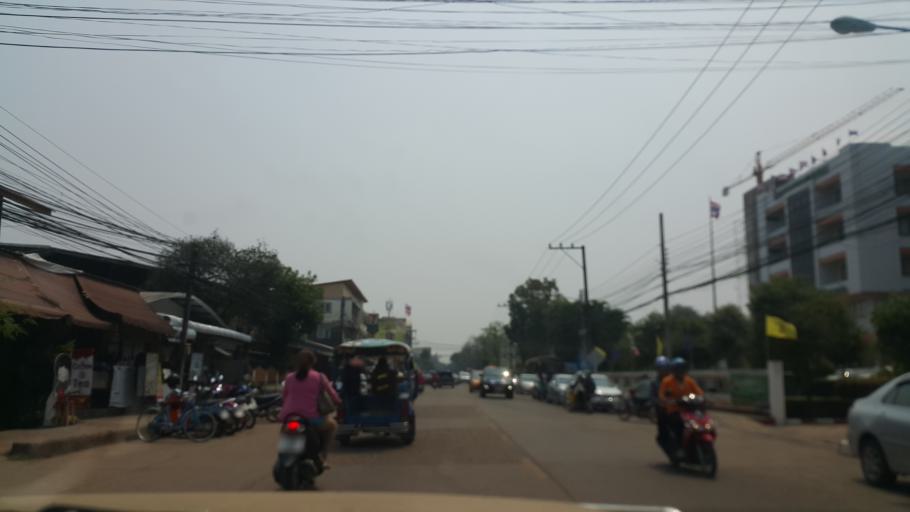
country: TH
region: Nakhon Phanom
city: Nakhon Phanom
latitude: 17.4146
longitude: 104.7778
